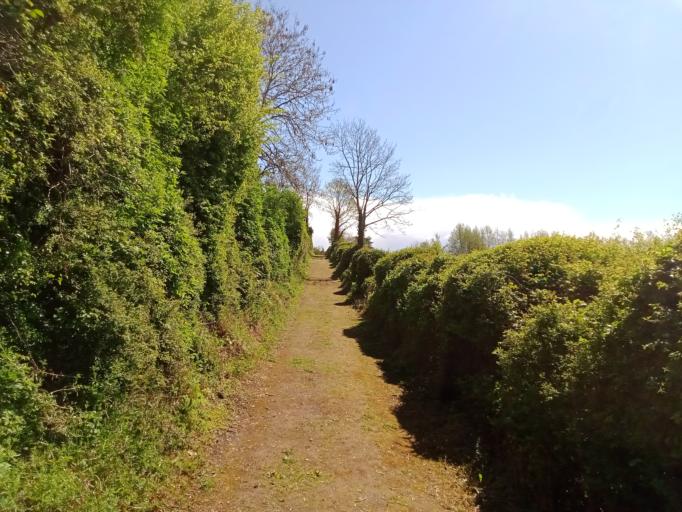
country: IE
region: Leinster
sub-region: Kilkenny
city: Kilkenny
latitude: 52.6904
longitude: -7.2600
